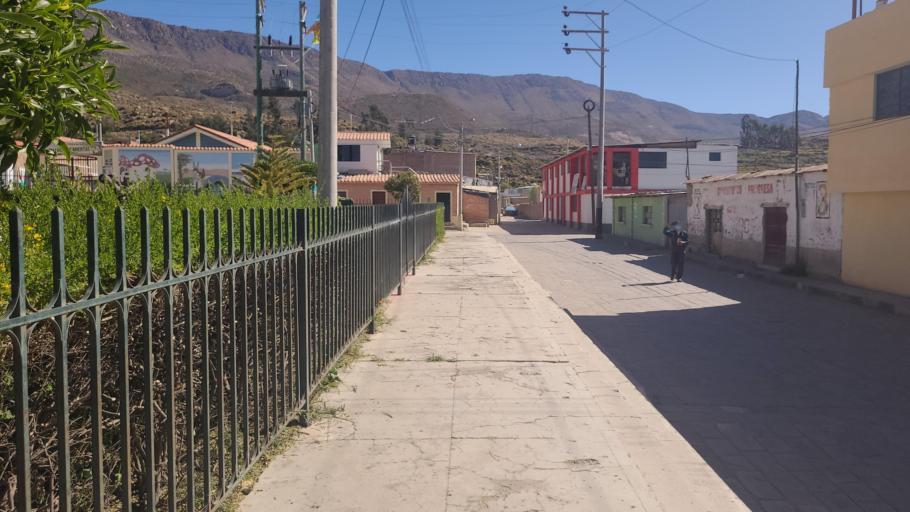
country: PE
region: Arequipa
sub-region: Provincia de Condesuyos
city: Chuquibamba
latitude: -15.8388
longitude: -72.6547
